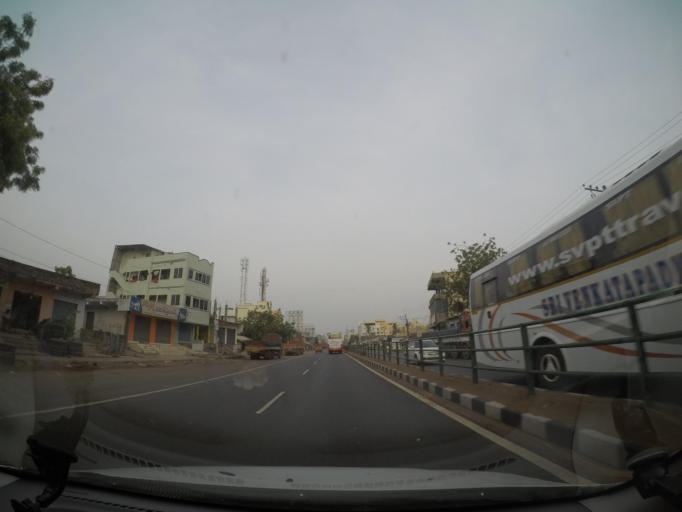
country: IN
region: Andhra Pradesh
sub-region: West Godavari
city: Eluru
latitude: 16.6362
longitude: 80.9750
